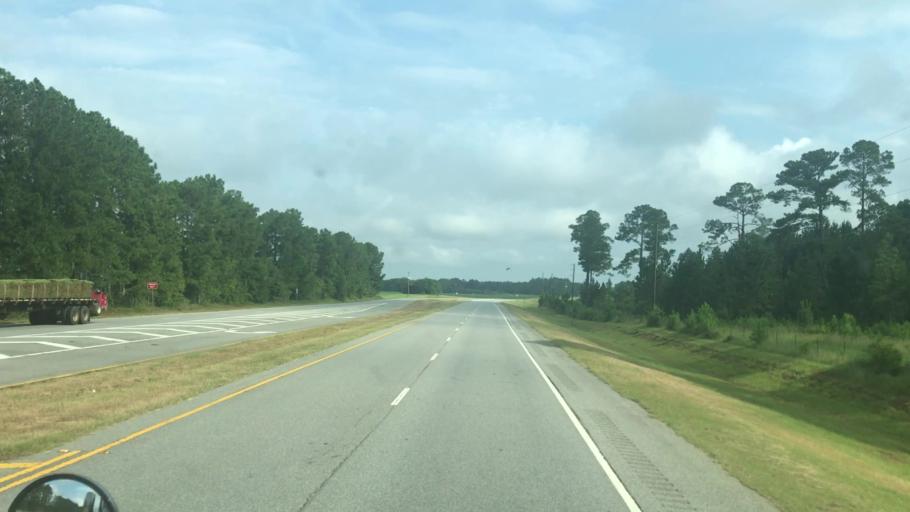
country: US
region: Georgia
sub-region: Miller County
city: Colquitt
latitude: 31.2130
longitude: -84.7757
